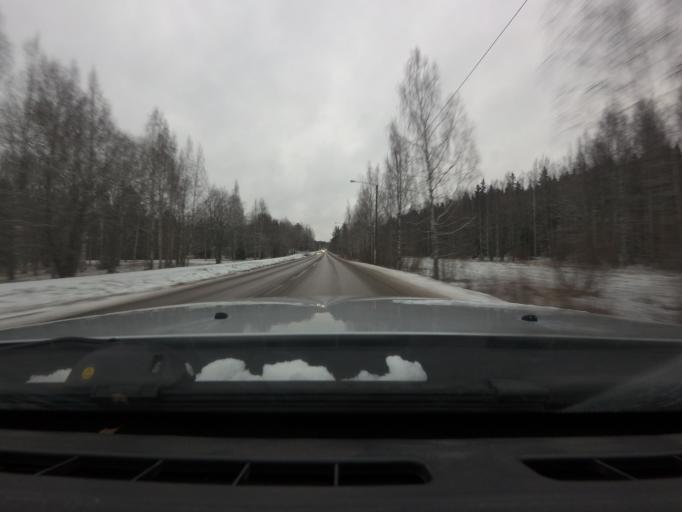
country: FI
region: Uusimaa
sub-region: Helsinki
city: Kauniainen
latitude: 60.2243
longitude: 24.7270
